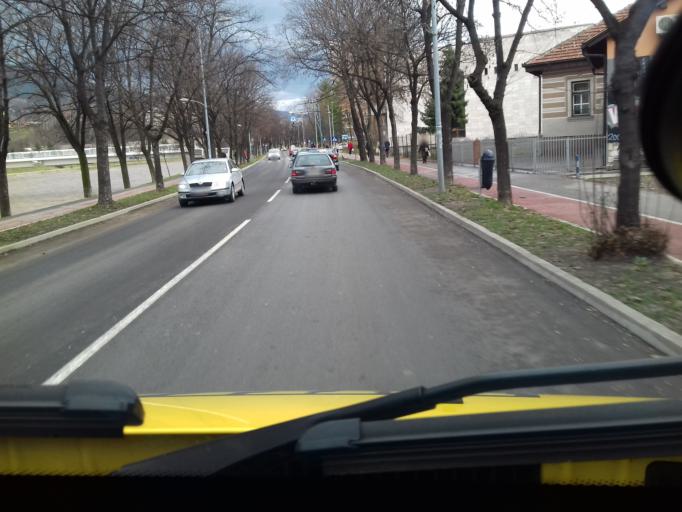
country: BA
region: Federation of Bosnia and Herzegovina
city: Zenica
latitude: 44.1999
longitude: 17.9122
